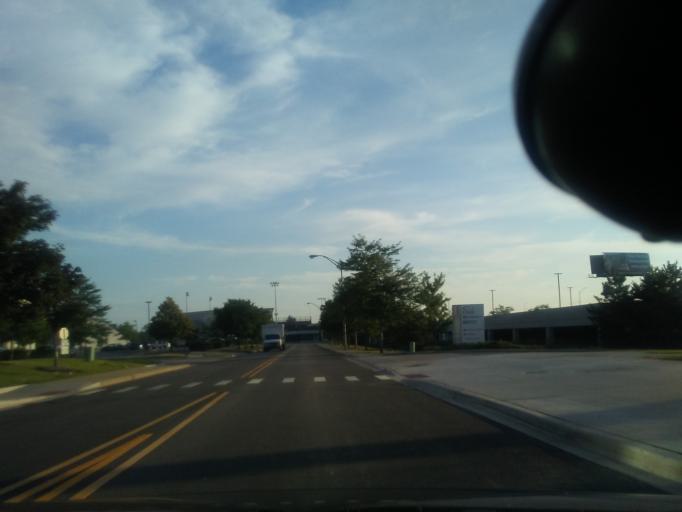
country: US
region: Illinois
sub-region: Cook County
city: Rosemont
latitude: 41.9787
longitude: -87.8722
